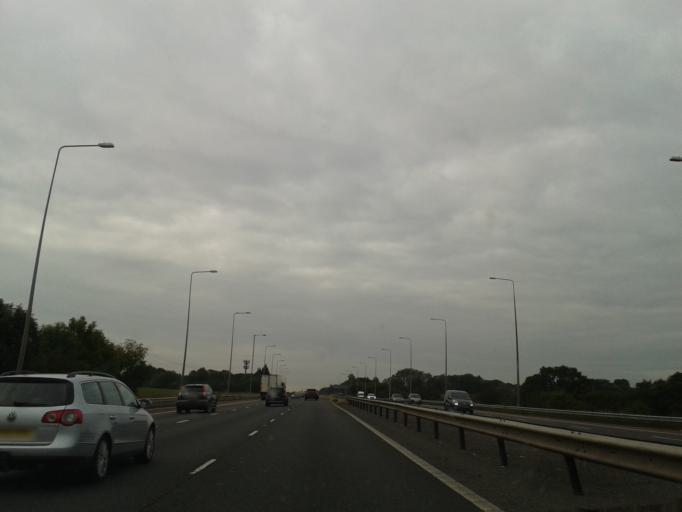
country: GB
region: England
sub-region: Borough of Wigan
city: Shevington
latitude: 53.6008
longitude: -2.6913
